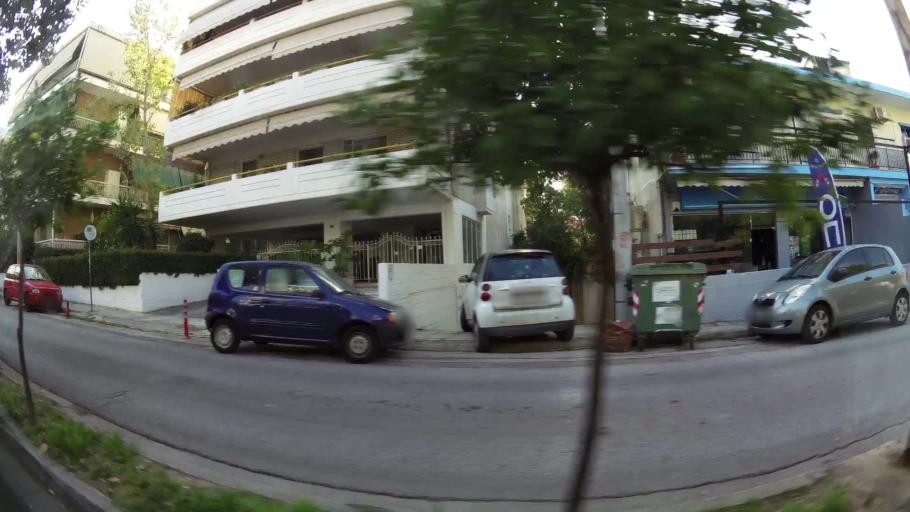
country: GR
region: Attica
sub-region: Nomarchia Athinas
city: Cholargos
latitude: 38.0052
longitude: 23.8076
